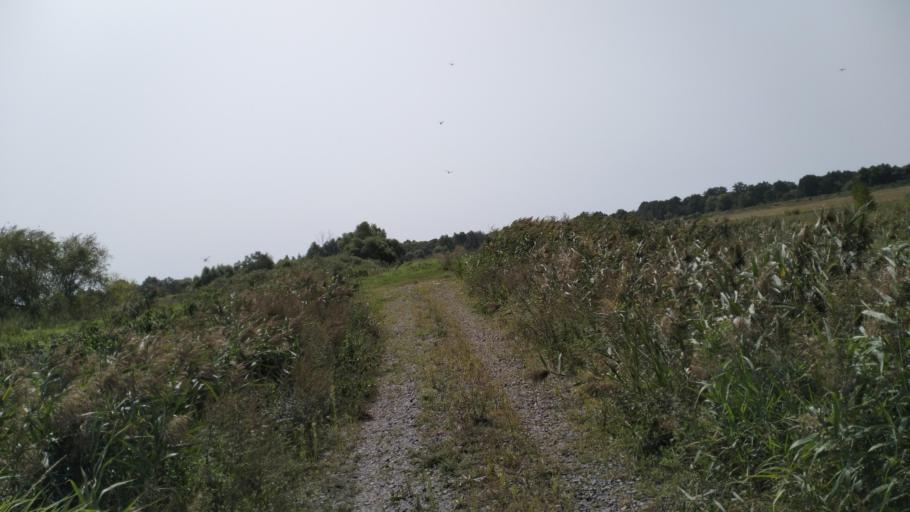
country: BY
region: Brest
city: Davyd-Haradok
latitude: 51.9685
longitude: 27.1735
